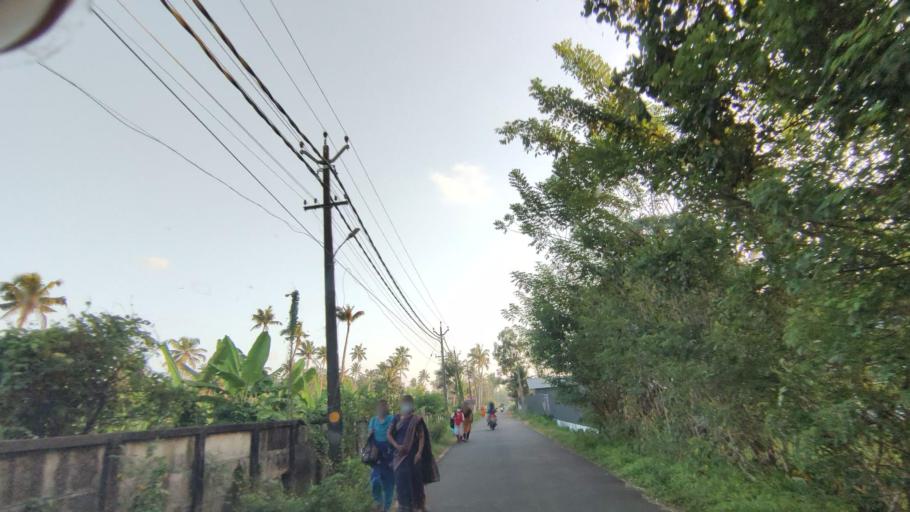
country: IN
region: Kerala
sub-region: Alappuzha
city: Shertallai
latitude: 9.6527
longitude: 76.3484
